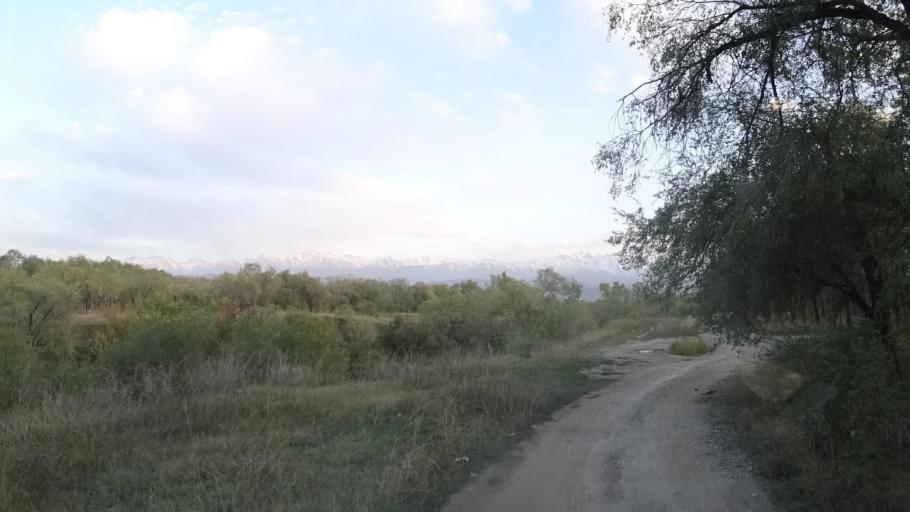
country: KZ
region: Almaty Oblysy
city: Pervomayskiy
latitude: 43.3357
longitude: 76.9991
